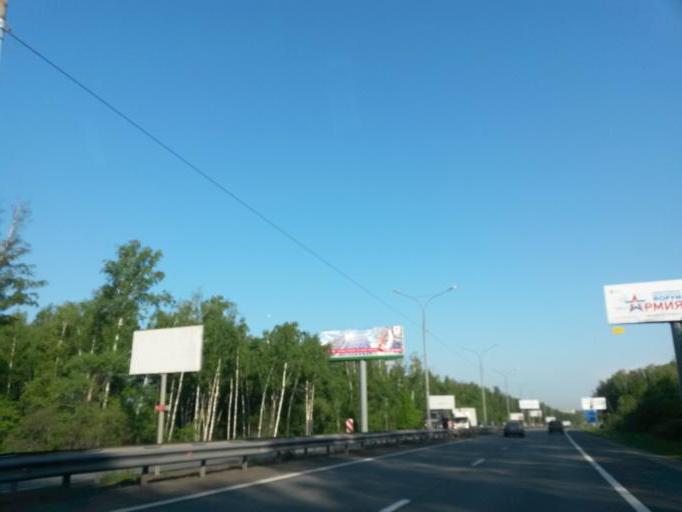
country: RU
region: Moskovskaya
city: Petrovskaya
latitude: 55.5521
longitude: 37.7871
